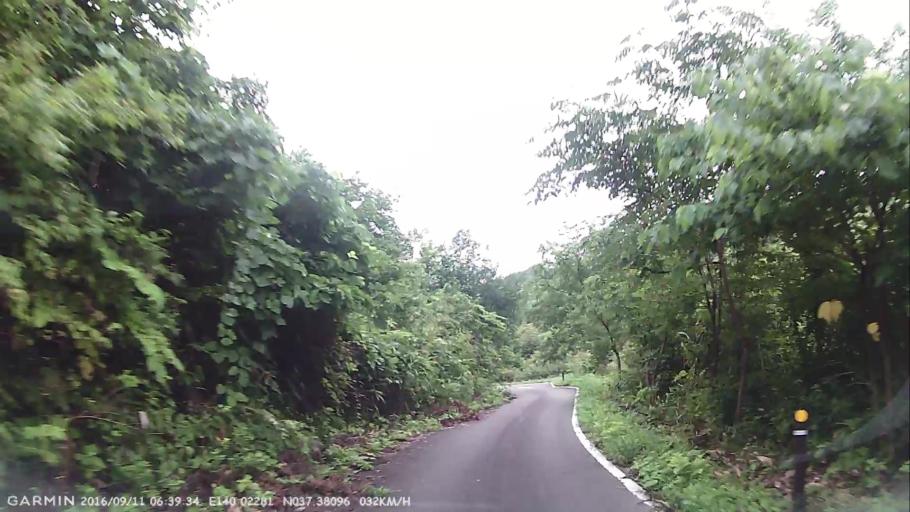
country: JP
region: Fukushima
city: Inawashiro
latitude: 37.3809
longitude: 140.0228
